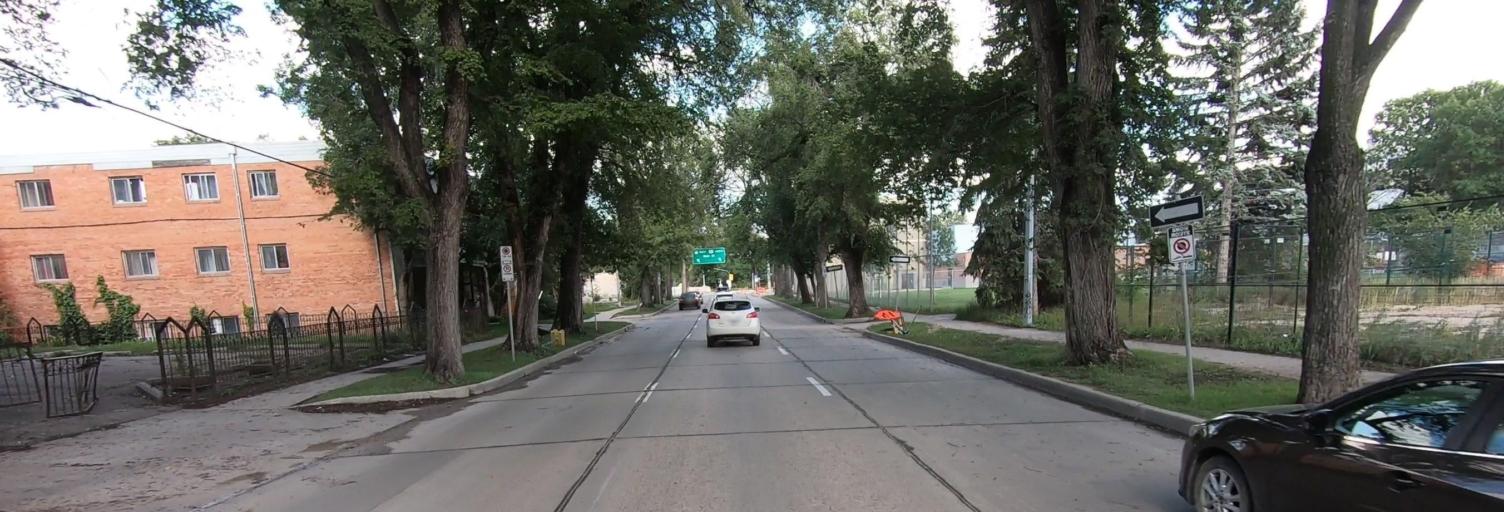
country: CA
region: Manitoba
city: Winnipeg
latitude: 49.8841
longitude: -97.1346
